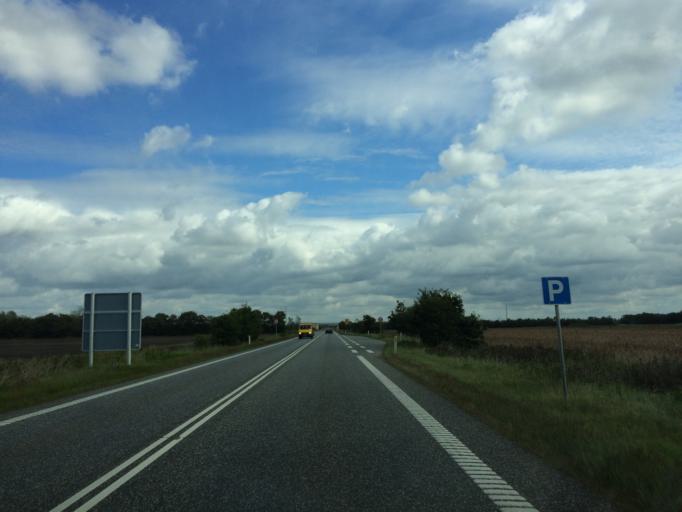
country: DK
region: Central Jutland
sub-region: Holstebro Kommune
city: Holstebro
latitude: 56.3669
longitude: 8.7115
